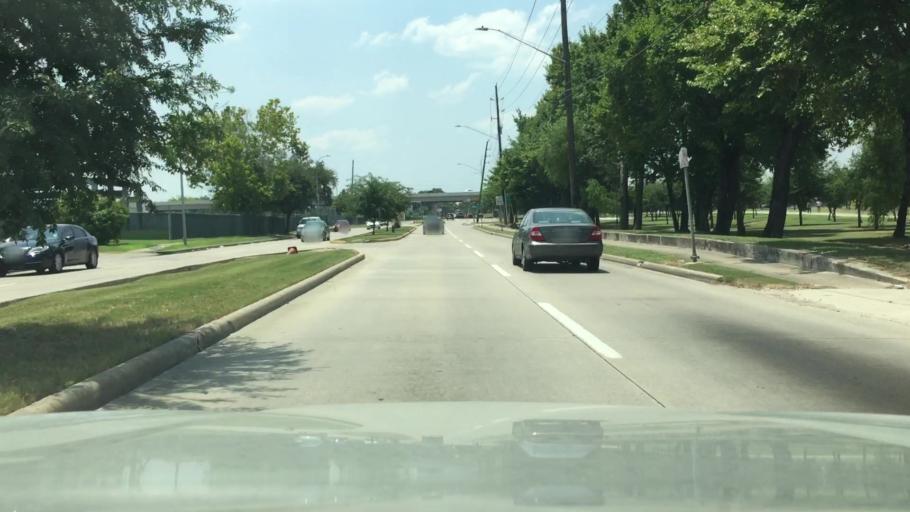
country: US
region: Texas
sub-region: Fort Bend County
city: Meadows Place
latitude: 29.7181
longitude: -95.5923
